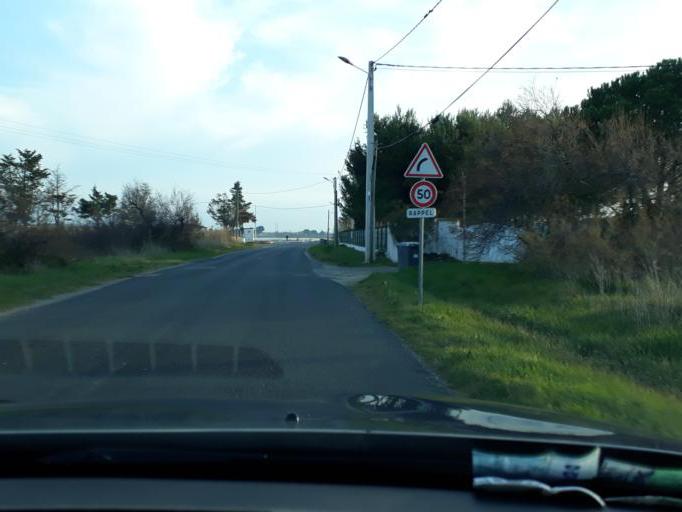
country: FR
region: Languedoc-Roussillon
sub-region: Departement de l'Herault
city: Marseillan
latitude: 43.3305
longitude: 3.5320
